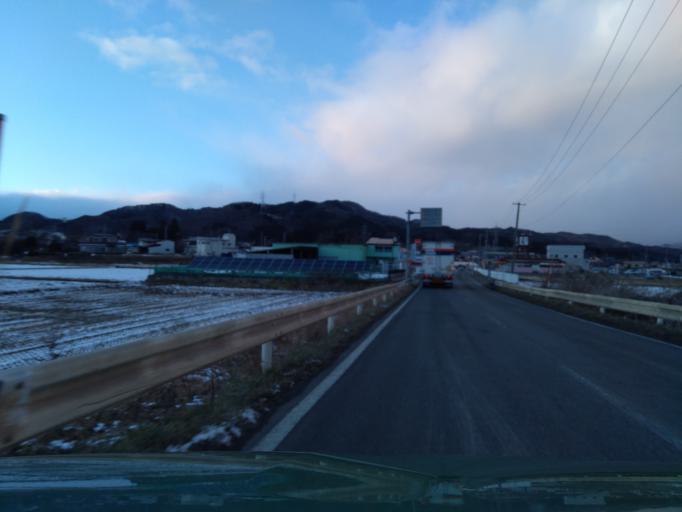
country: JP
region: Iwate
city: Shizukuishi
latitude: 39.6981
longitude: 141.0631
